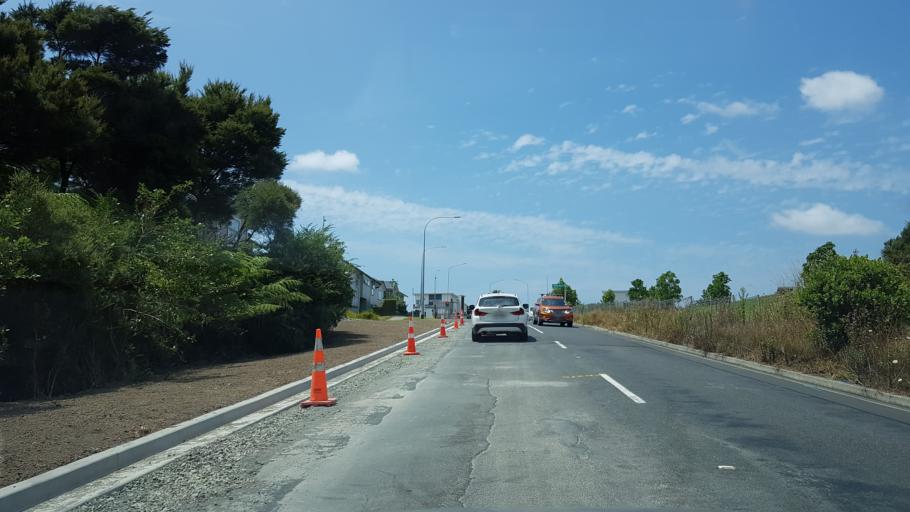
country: NZ
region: Auckland
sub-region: Auckland
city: Rosebank
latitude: -36.7934
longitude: 174.6540
